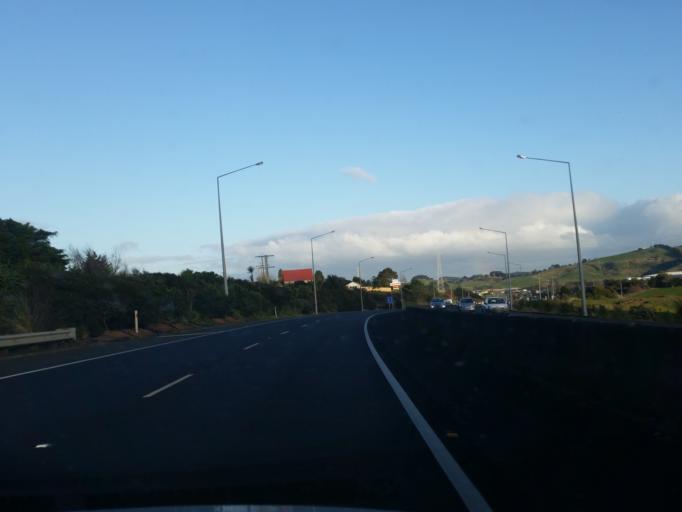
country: NZ
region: Auckland
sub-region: Auckland
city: Pukekohe East
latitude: -37.2337
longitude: 175.0198
